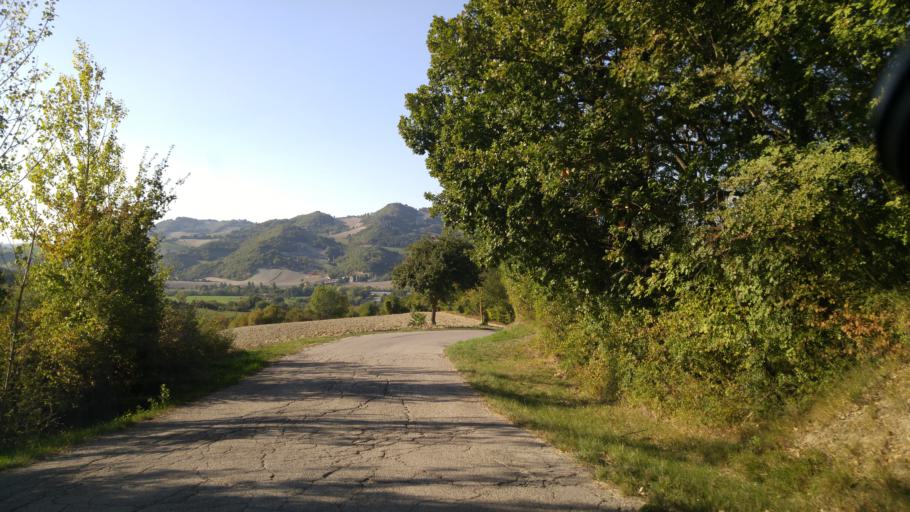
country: IT
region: The Marches
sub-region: Provincia di Pesaro e Urbino
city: Fermignano
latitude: 43.6628
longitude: 12.6498
